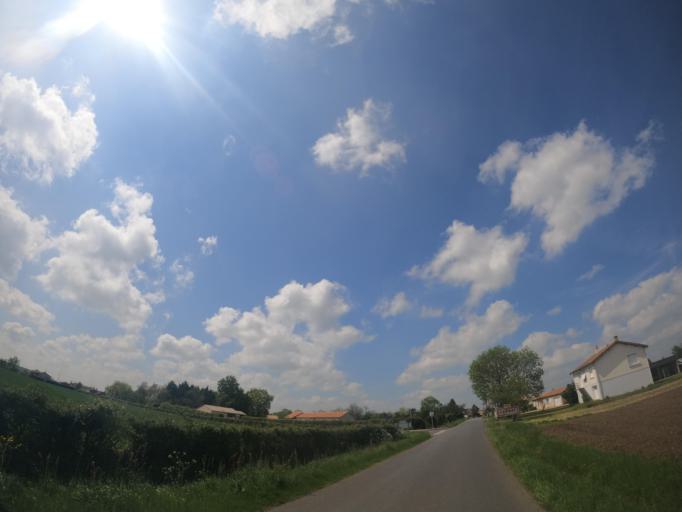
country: FR
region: Poitou-Charentes
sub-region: Departement des Deux-Sevres
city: Saint-Varent
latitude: 46.8590
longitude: -0.2407
